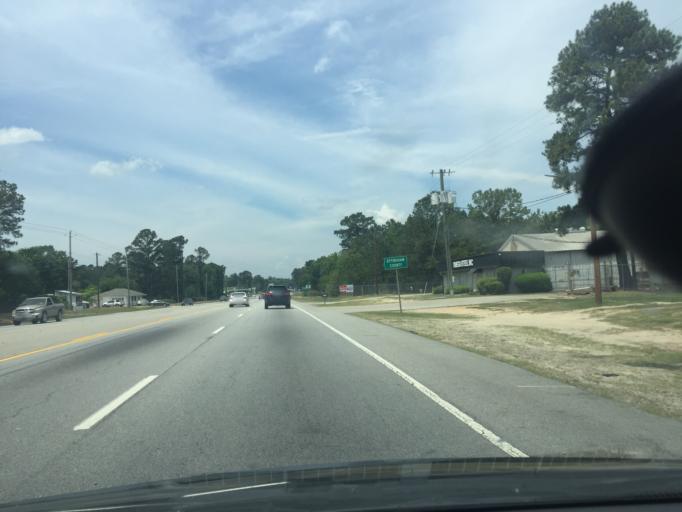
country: US
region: Georgia
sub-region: Chatham County
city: Bloomingdale
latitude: 32.1417
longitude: -81.3276
